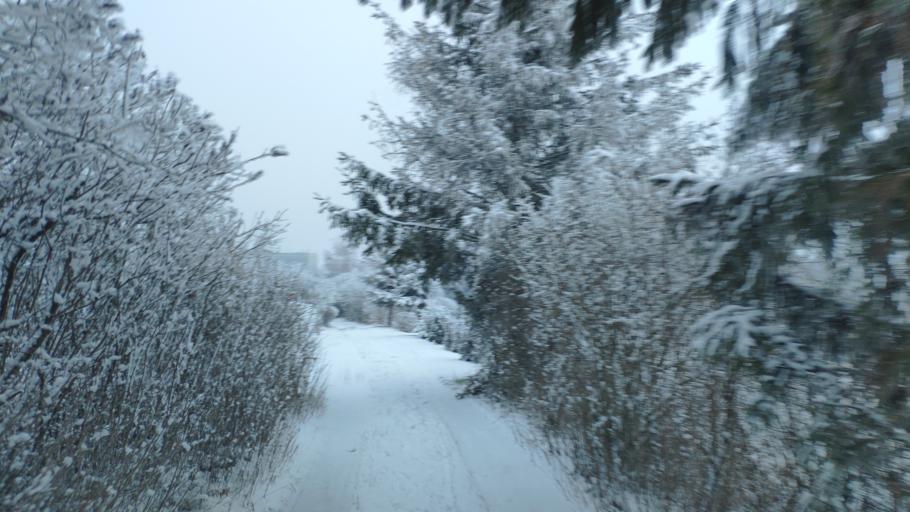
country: SK
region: Kosicky
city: Kosice
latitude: 48.6459
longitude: 21.1685
